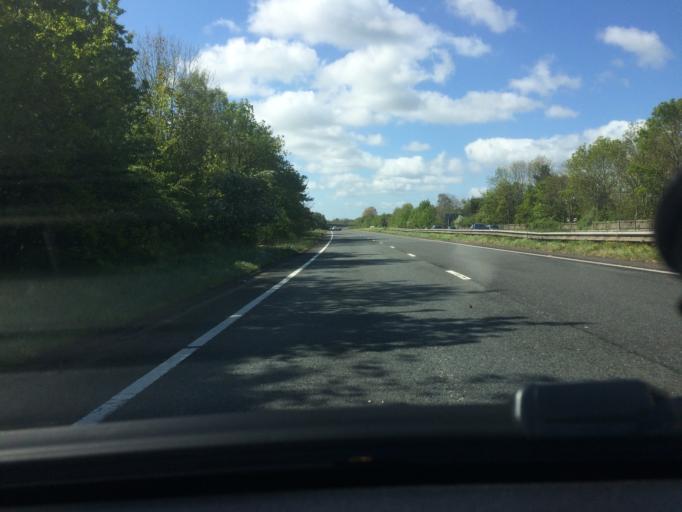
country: GB
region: England
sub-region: Cheshire West and Chester
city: Hoole
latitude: 53.1781
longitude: -2.8568
